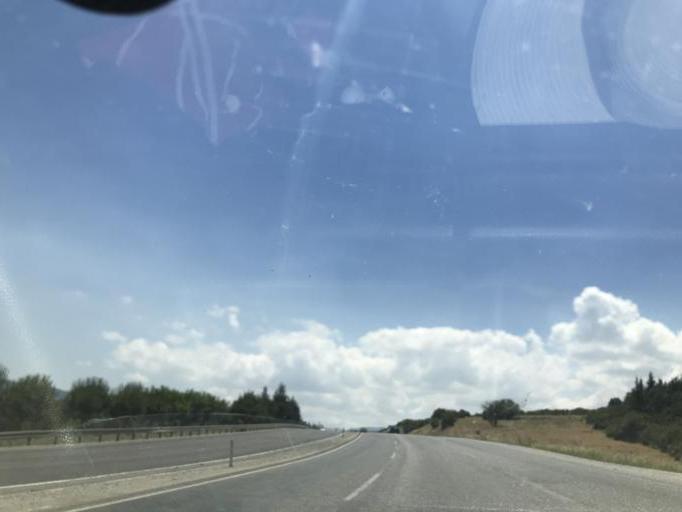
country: TR
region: Denizli
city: Honaz
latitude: 37.7104
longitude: 29.2047
